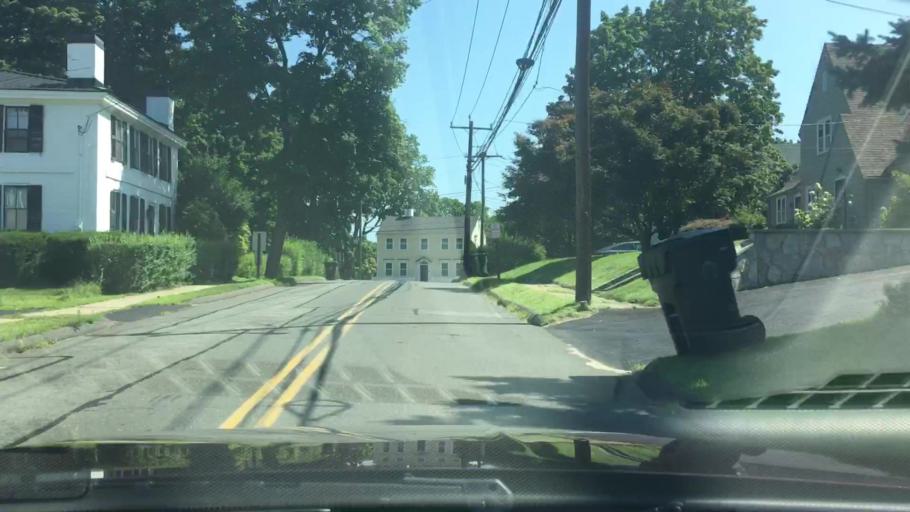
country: US
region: Connecticut
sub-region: Hartford County
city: Kensington
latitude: 41.6177
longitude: -72.7474
